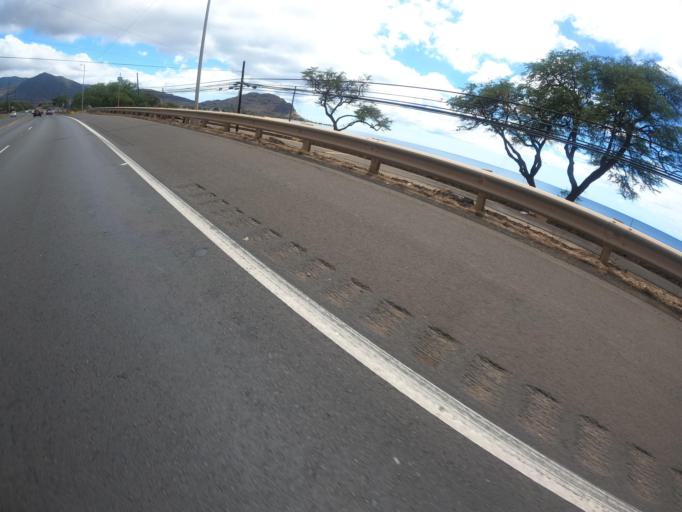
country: US
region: Hawaii
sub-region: Honolulu County
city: Waianae
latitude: 21.4300
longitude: -158.1819
